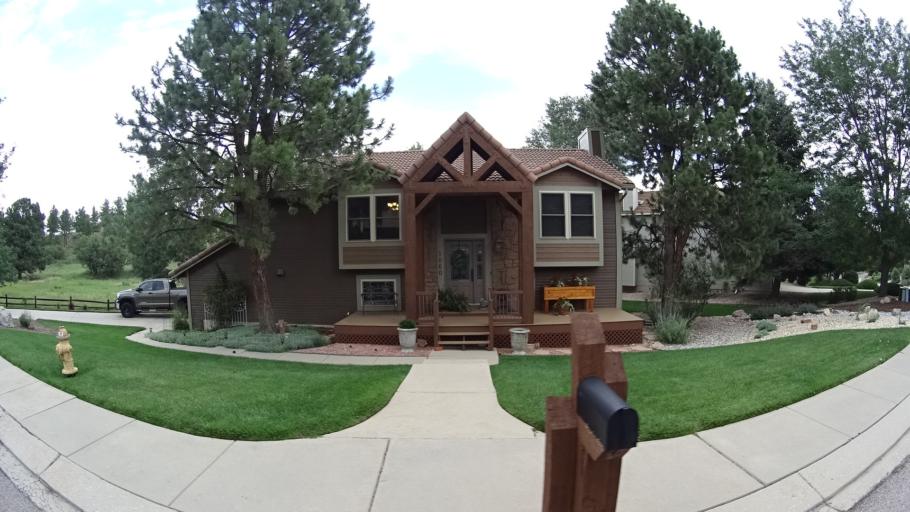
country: US
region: Colorado
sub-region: El Paso County
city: Colorado Springs
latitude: 38.9108
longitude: -104.8475
